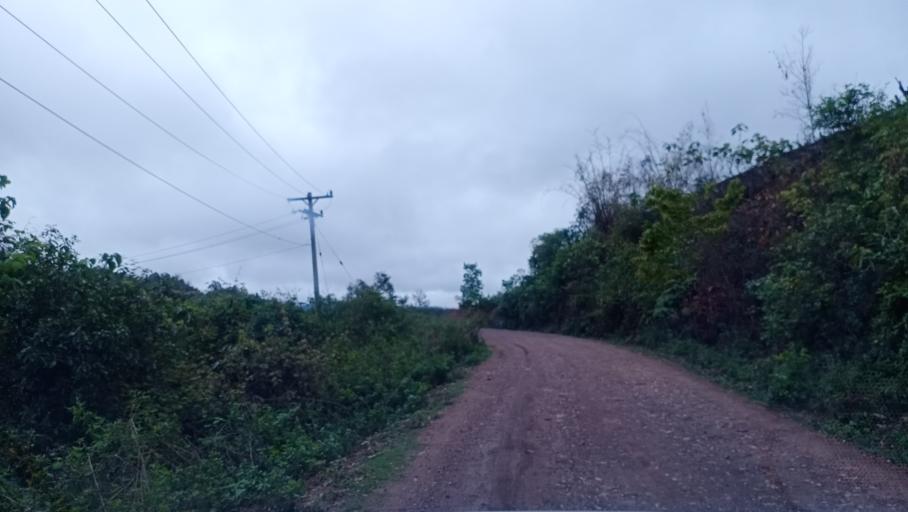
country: LA
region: Phongsali
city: Phongsali
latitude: 21.3424
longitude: 102.0873
